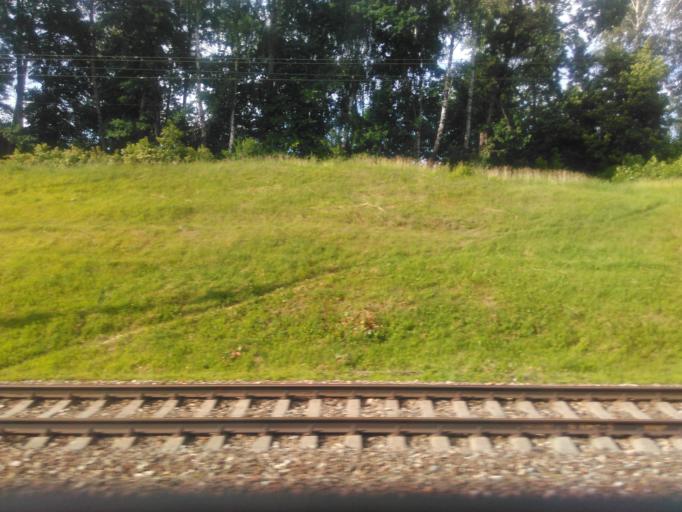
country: RU
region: Moskovskaya
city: Saltykovka
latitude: 55.7549
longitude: 37.9391
